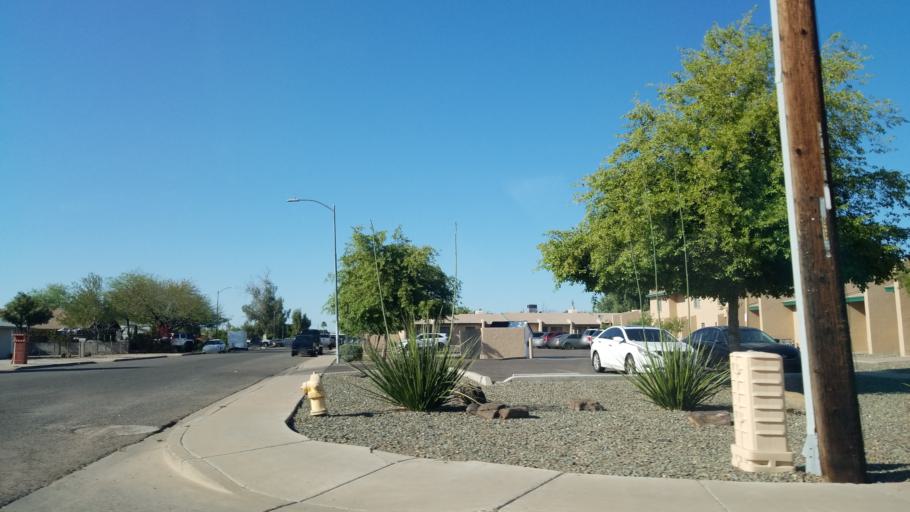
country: US
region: Arizona
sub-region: Maricopa County
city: Glendale
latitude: 33.5313
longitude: -112.1737
